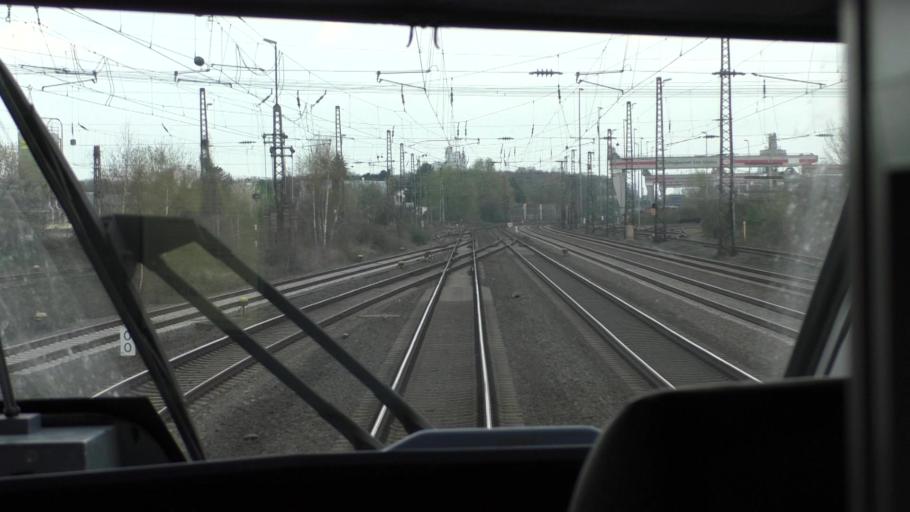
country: DE
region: North Rhine-Westphalia
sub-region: Regierungsbezirk Koln
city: Hurth
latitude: 50.8803
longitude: 6.9121
